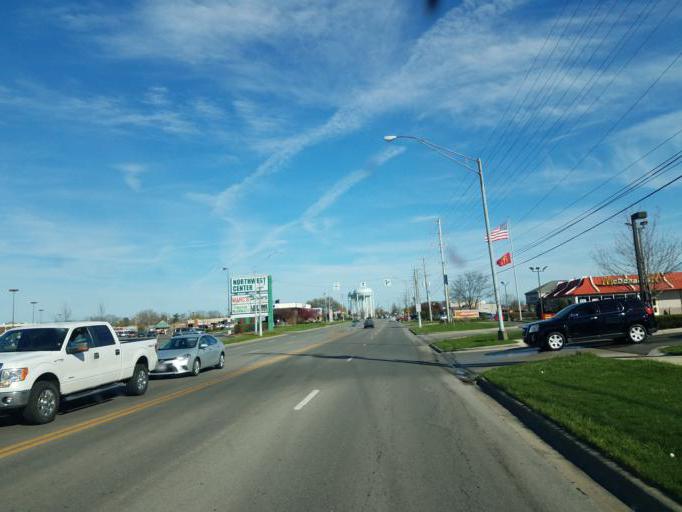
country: US
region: Ohio
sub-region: Franklin County
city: Dublin
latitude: 40.0554
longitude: -83.0709
